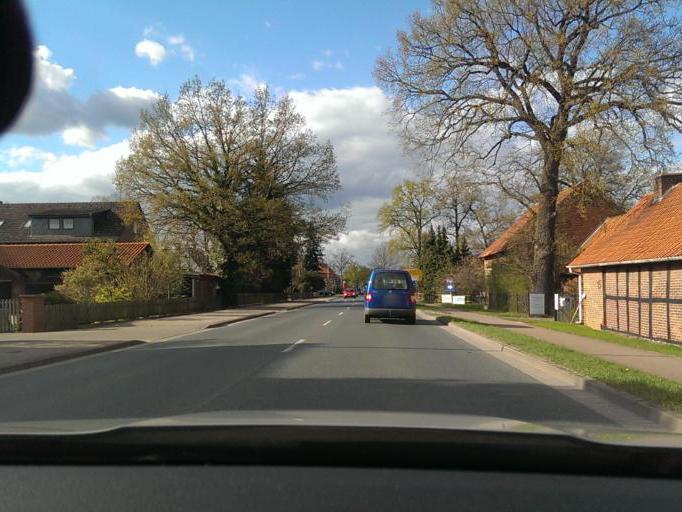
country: DE
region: Lower Saxony
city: Elze
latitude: 52.5433
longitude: 9.7274
